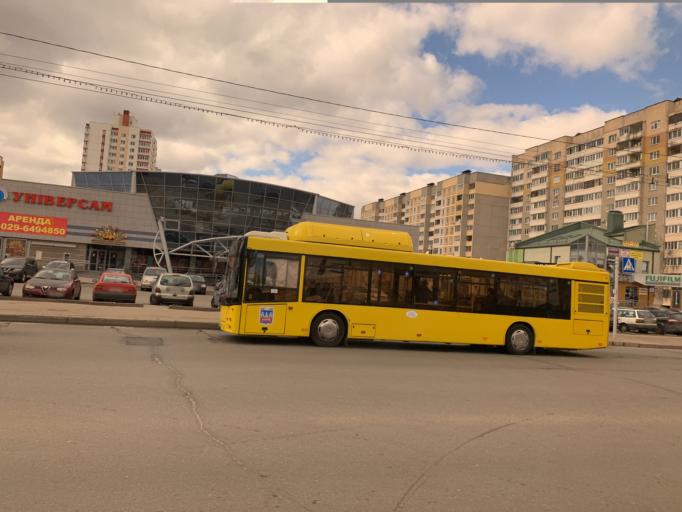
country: BY
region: Minsk
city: Borovlyany
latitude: 53.9386
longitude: 27.6873
